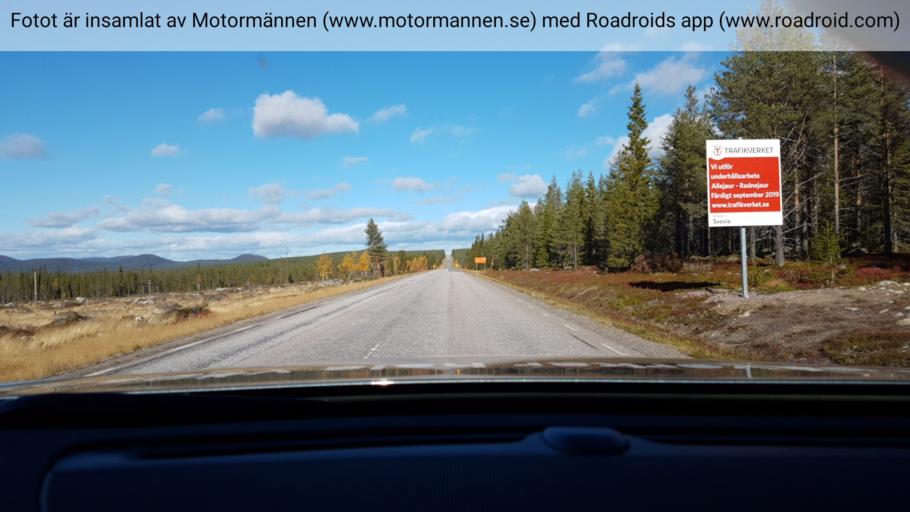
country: SE
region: Norrbotten
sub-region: Arjeplogs Kommun
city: Arjeplog
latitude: 65.8168
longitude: 18.4446
